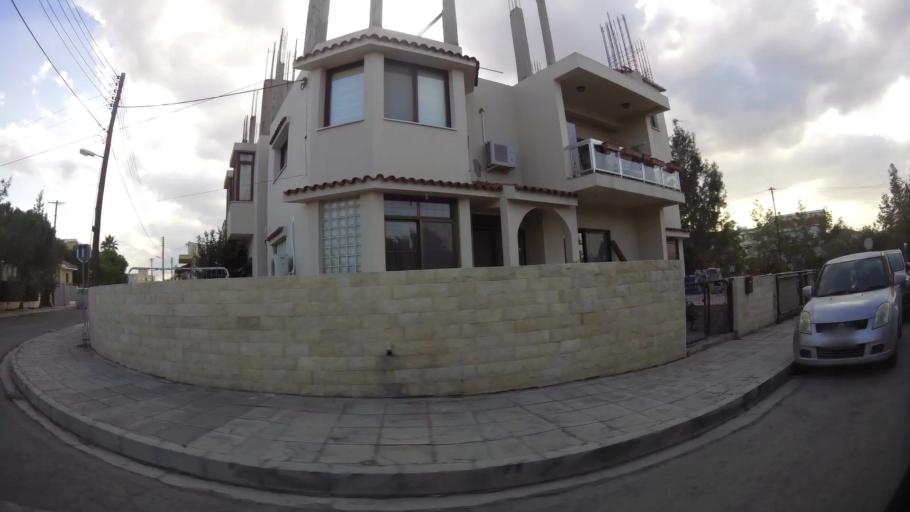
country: CY
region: Lefkosia
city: Kato Deftera
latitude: 35.1117
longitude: 33.3024
